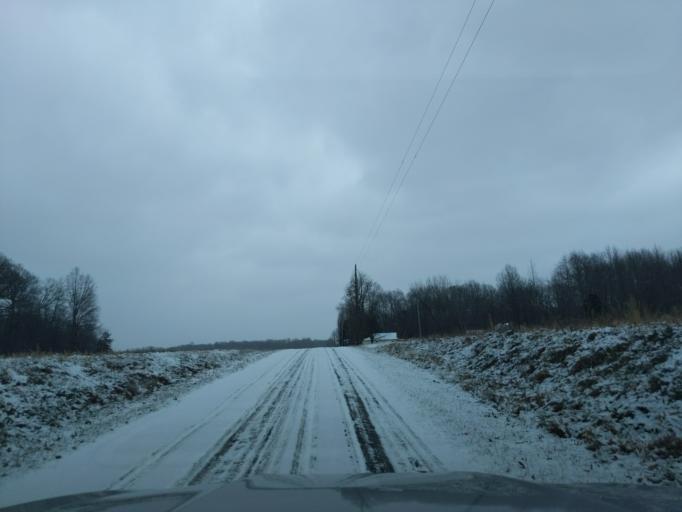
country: US
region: Indiana
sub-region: Decatur County
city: Westport
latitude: 39.2049
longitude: -85.5166
